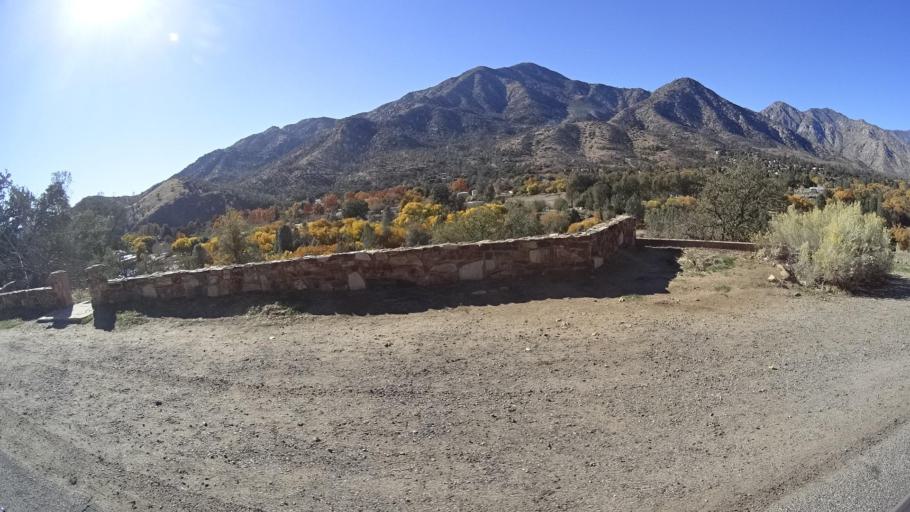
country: US
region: California
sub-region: Kern County
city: Kernville
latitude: 35.7595
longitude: -118.4204
